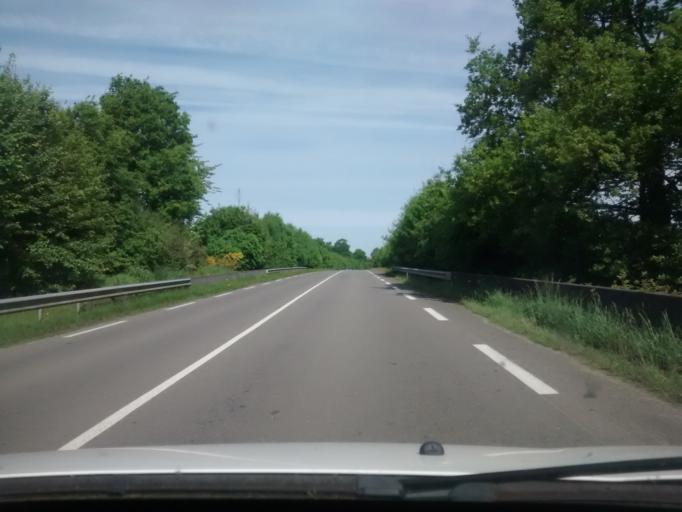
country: FR
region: Brittany
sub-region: Departement d'Ille-et-Vilaine
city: Saint-Brice-en-Cogles
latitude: 48.4107
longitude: -1.3836
